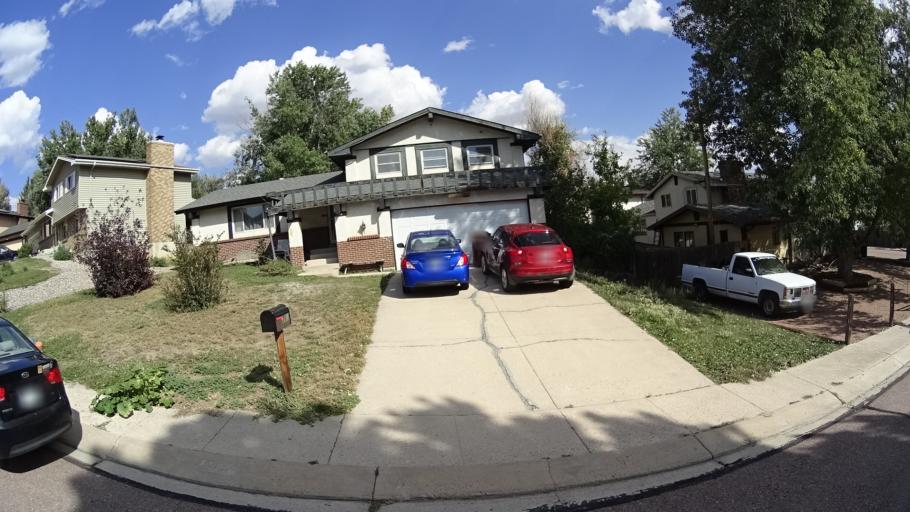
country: US
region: Colorado
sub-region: El Paso County
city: Cimarron Hills
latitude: 38.8700
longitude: -104.7311
